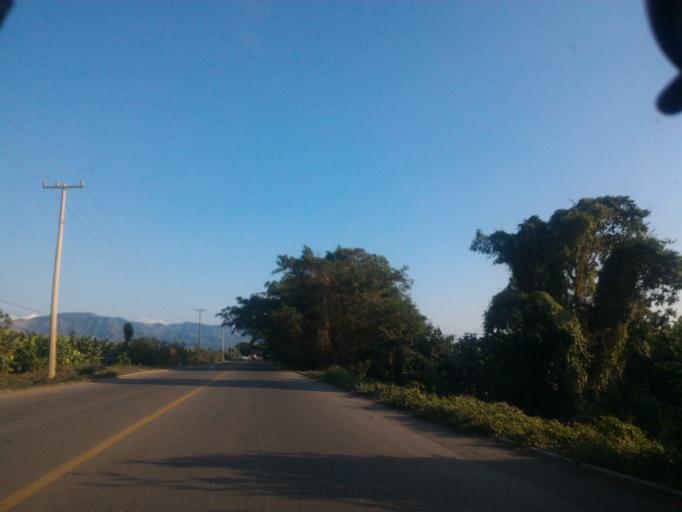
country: MX
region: Michoacan
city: Coahuayana Viejo
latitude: 18.7132
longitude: -103.7128
